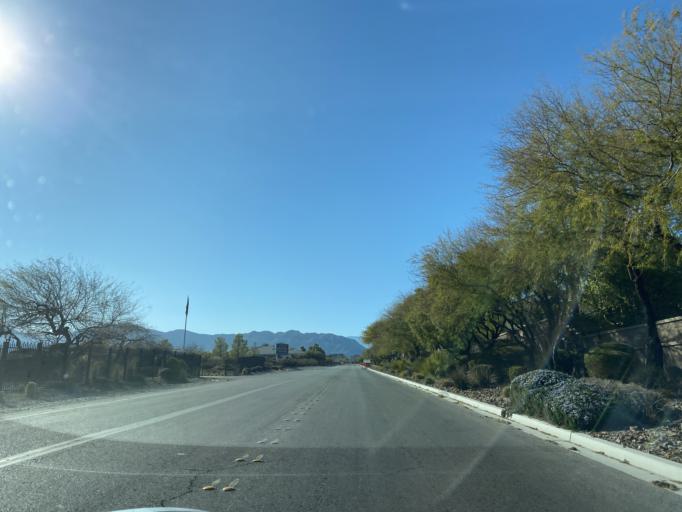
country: US
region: Nevada
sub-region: Clark County
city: Summerlin South
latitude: 36.2957
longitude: -115.3091
